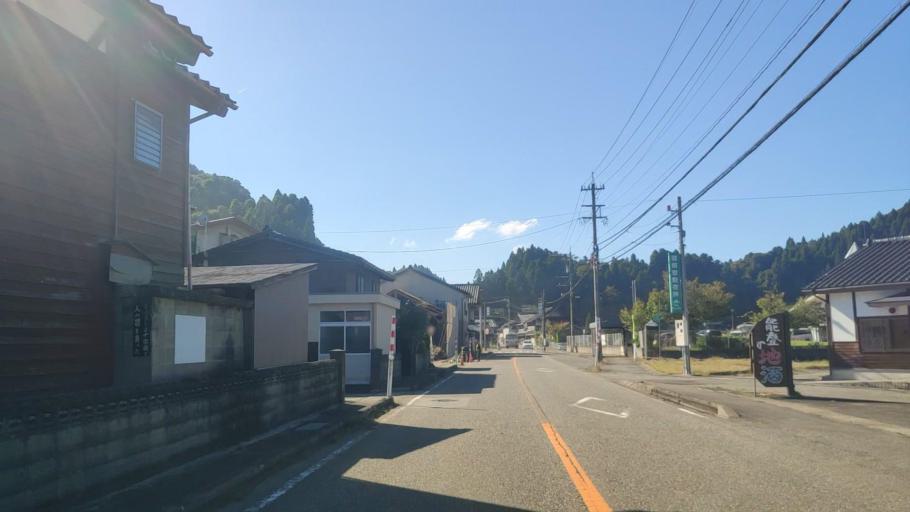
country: JP
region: Ishikawa
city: Nanao
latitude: 37.2815
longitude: 137.0417
